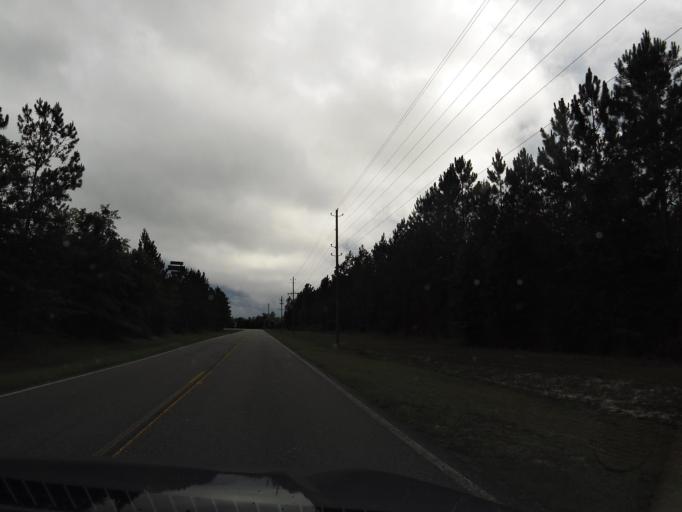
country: US
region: Georgia
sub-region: Camden County
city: Kingsland
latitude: 30.7662
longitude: -81.6493
